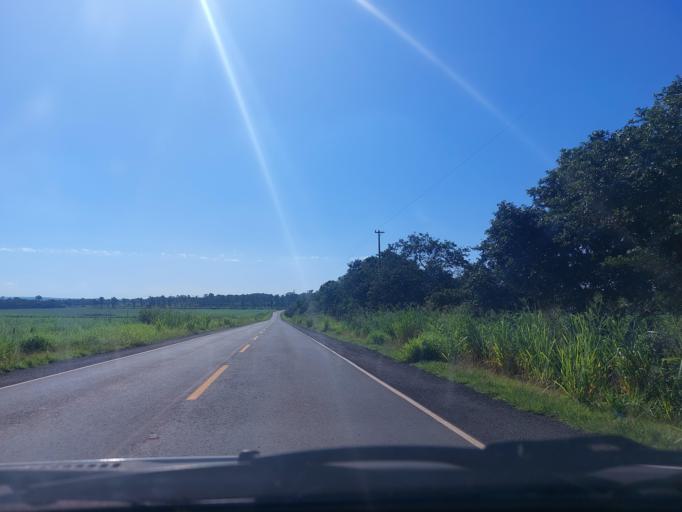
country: PY
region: San Pedro
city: Guayaybi
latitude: -24.3212
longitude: -56.1856
